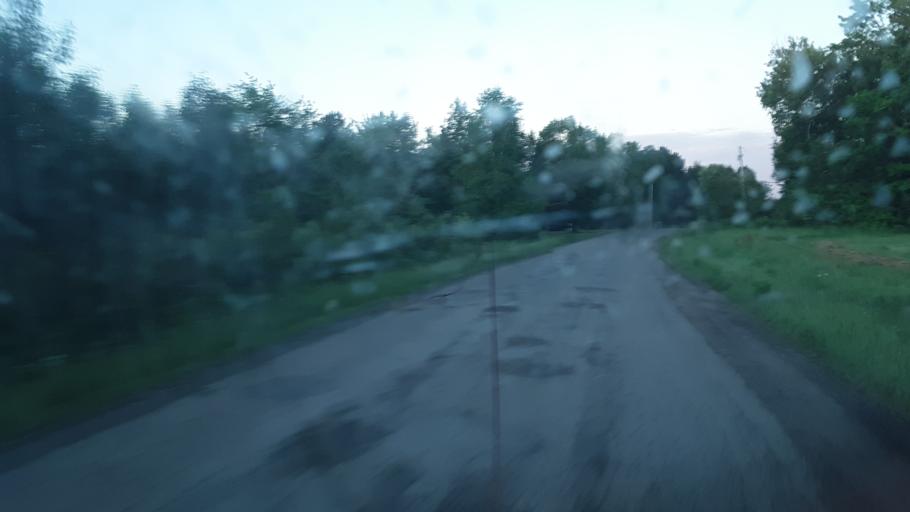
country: US
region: Maine
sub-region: Aroostook County
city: Caribou
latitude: 46.8720
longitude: -68.1216
